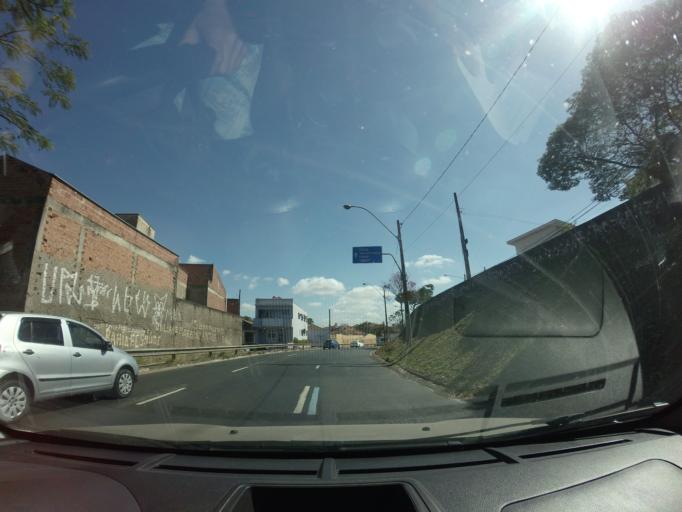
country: BR
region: Sao Paulo
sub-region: Piracicaba
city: Piracicaba
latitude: -22.7196
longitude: -47.6461
